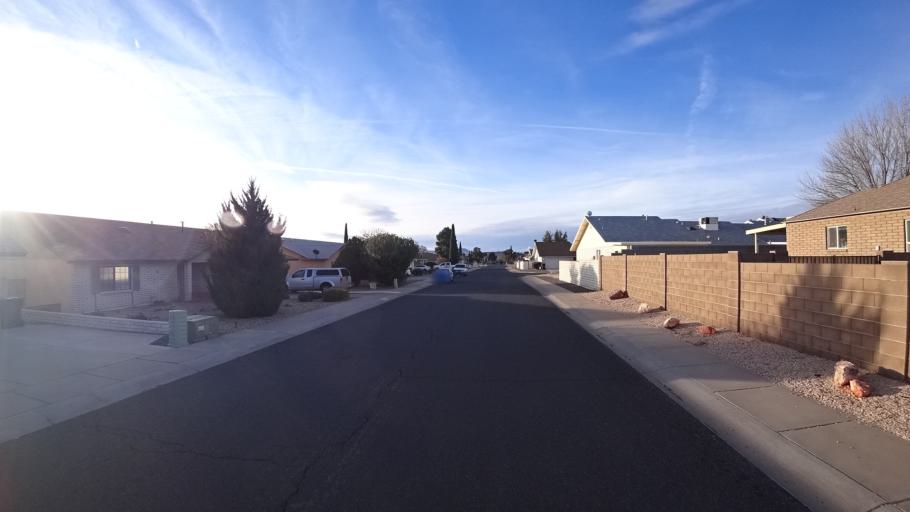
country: US
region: Arizona
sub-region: Mohave County
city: New Kingman-Butler
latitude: 35.2428
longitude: -114.0413
